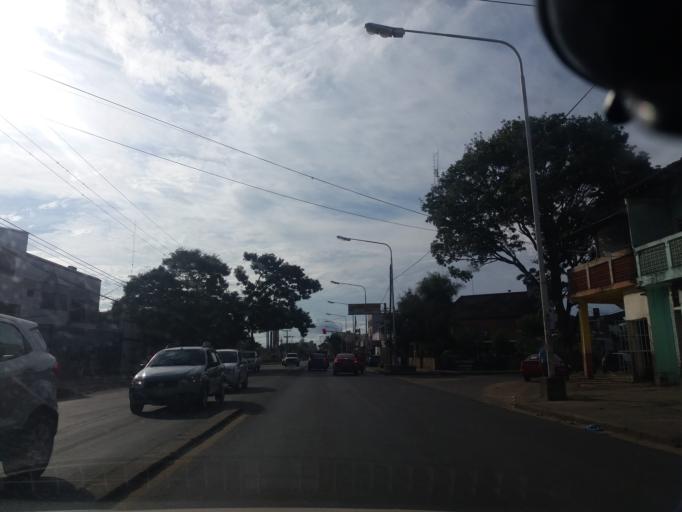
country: AR
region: Corrientes
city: Corrientes
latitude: -27.4849
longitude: -58.8243
